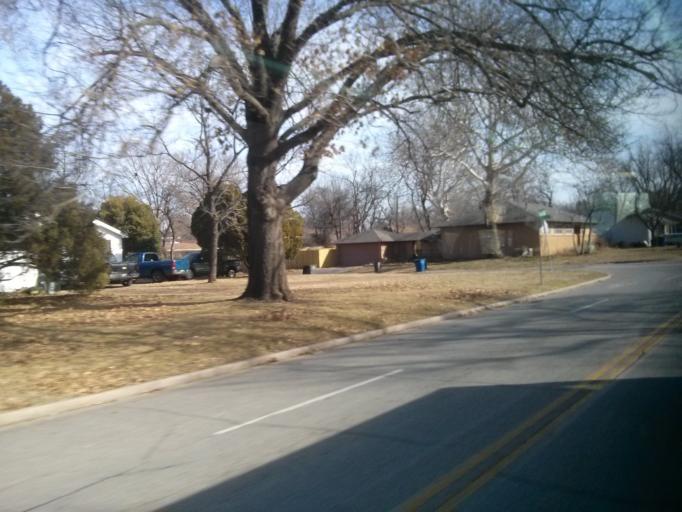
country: US
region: Oklahoma
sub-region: Tulsa County
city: Tulsa
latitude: 36.1559
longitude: -95.9364
